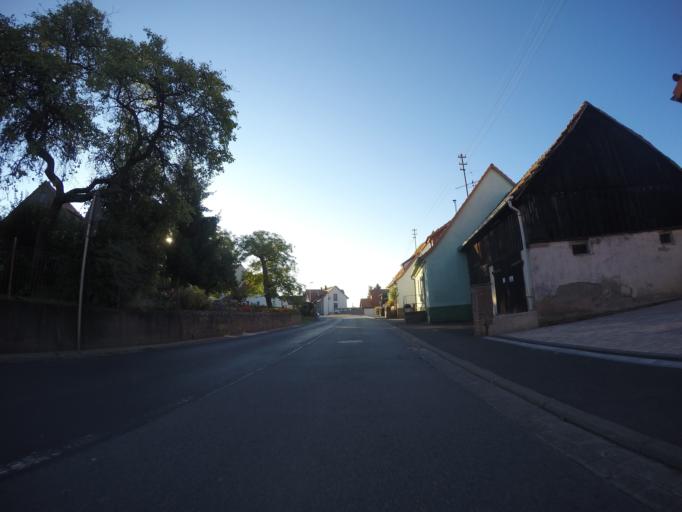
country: DE
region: Bavaria
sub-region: Regierungsbezirk Unterfranken
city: Schollbrunn
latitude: 49.8339
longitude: 9.4662
